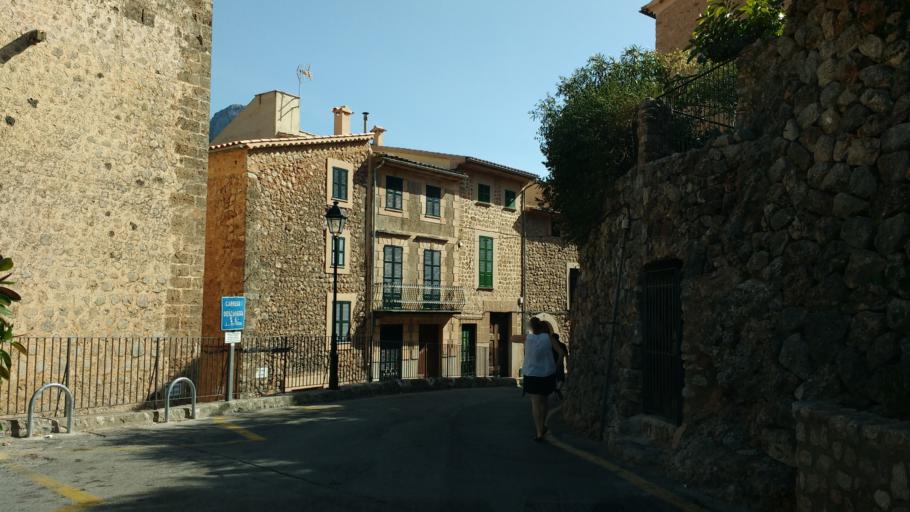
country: ES
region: Balearic Islands
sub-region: Illes Balears
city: Fornalutx
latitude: 39.7828
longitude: 2.7416
